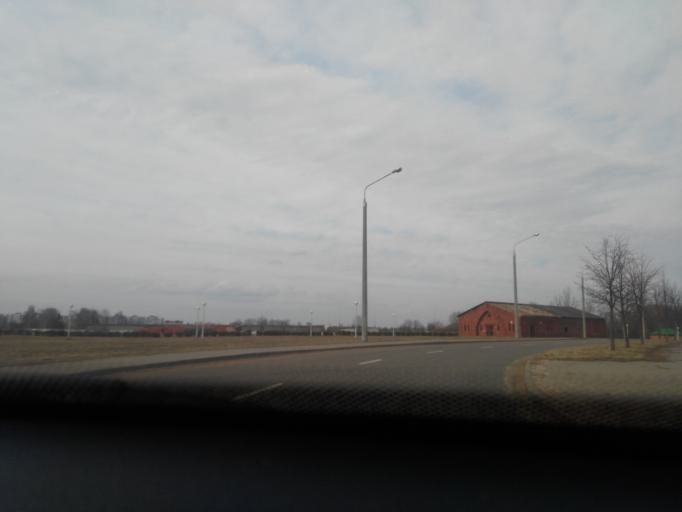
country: BY
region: Mogilev
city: Babruysk
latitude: 53.1429
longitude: 29.2512
